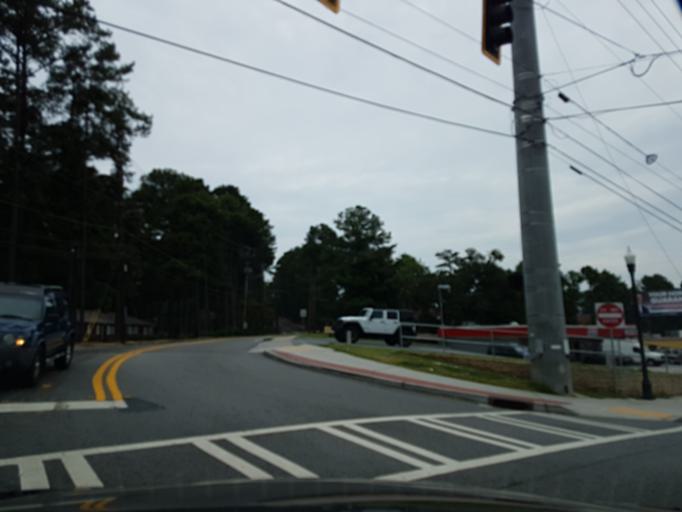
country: US
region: Georgia
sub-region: DeKalb County
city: North Atlanta
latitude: 33.8443
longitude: -84.3274
